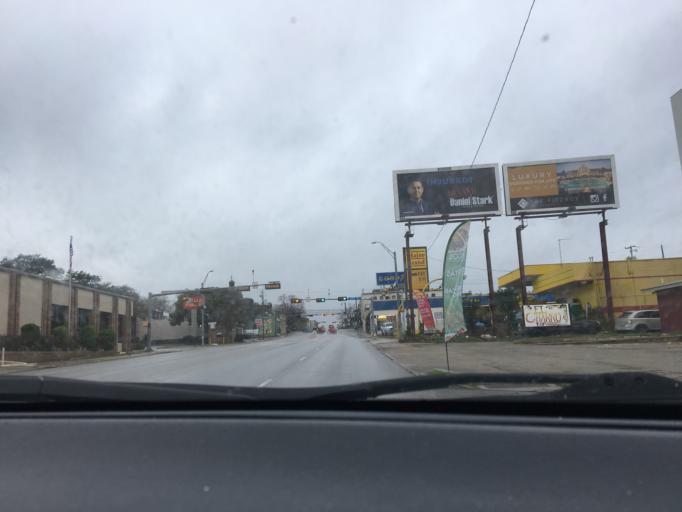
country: US
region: Texas
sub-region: Hays County
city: San Marcos
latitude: 29.8836
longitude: -97.9381
